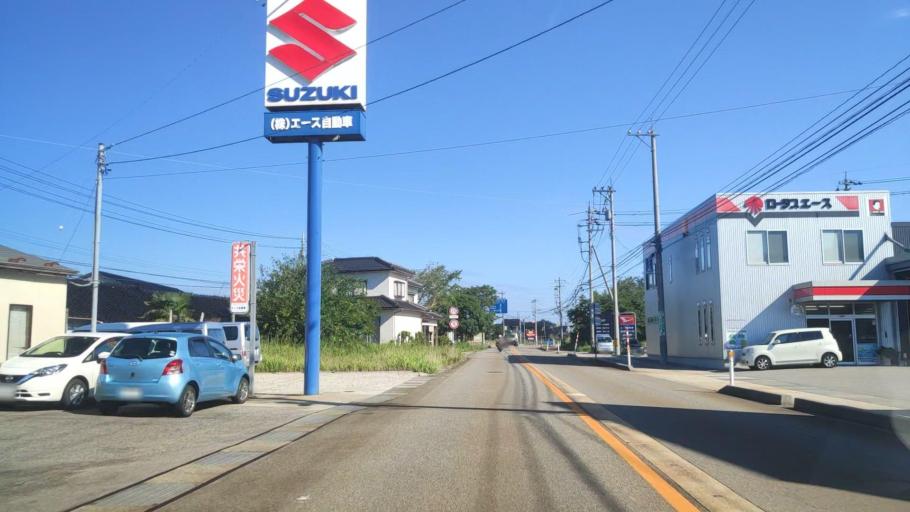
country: JP
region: Ishikawa
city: Hakui
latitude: 36.9948
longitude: 136.7767
